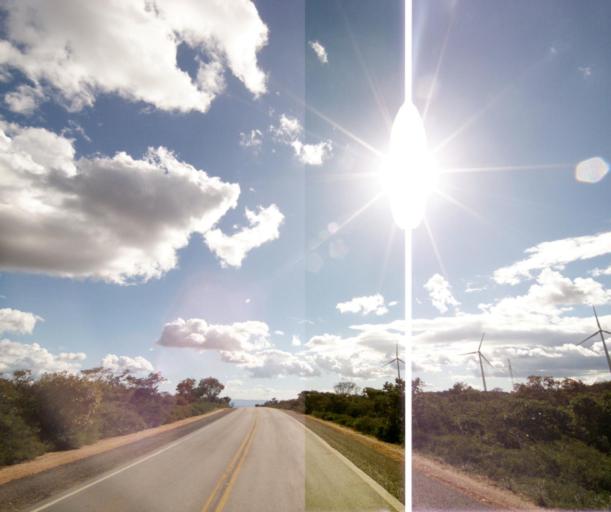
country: BR
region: Bahia
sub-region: Caetite
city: Caetite
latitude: -14.1176
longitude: -42.6067
